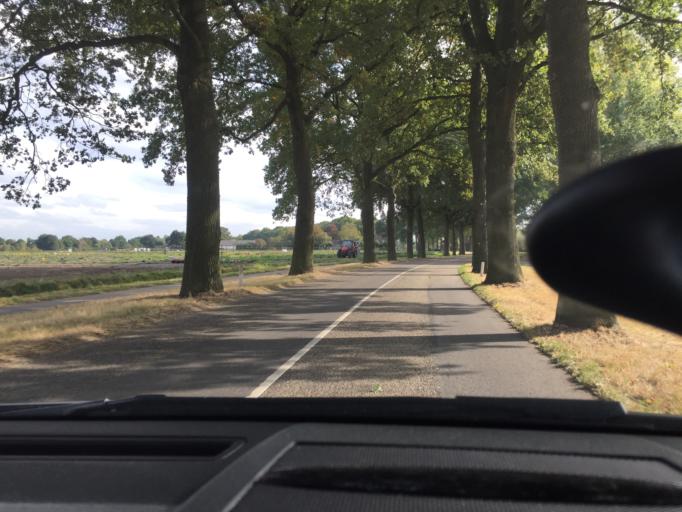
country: NL
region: North Brabant
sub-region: Gemeente Laarbeek
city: Aarle-Rixtel
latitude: 51.5101
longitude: 5.6182
